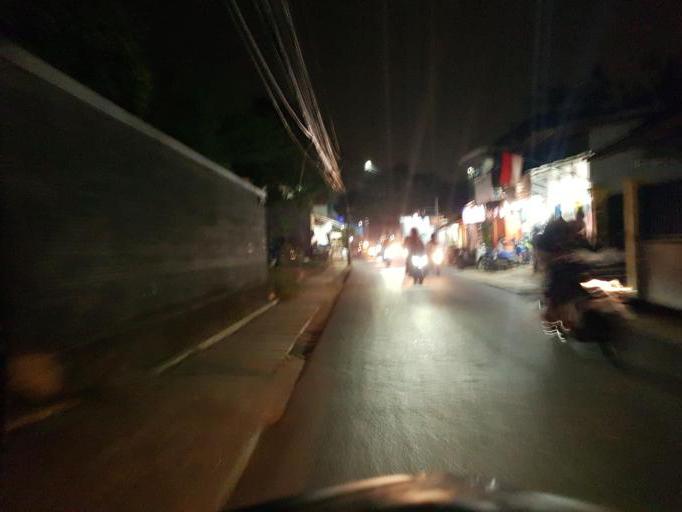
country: ID
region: West Java
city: Cileungsir
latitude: -6.3156
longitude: 106.9154
